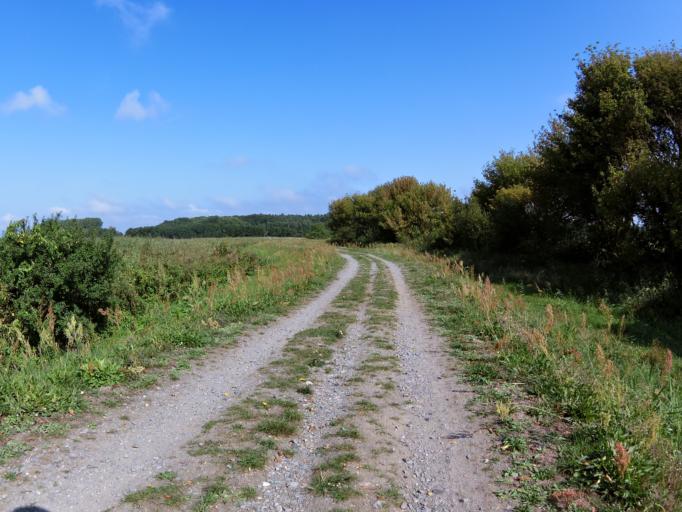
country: DE
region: Mecklenburg-Vorpommern
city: Loddin
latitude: 53.9942
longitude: 14.0472
